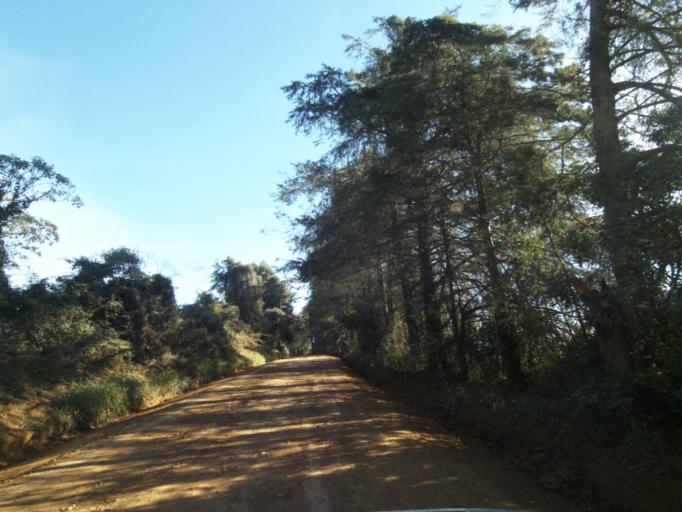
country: BR
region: Parana
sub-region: Tibagi
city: Tibagi
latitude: -24.5280
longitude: -50.5111
